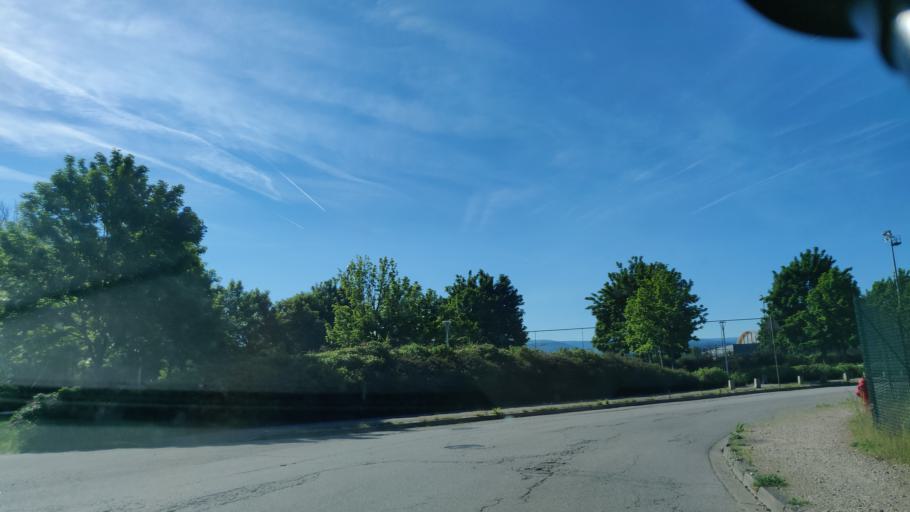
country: FR
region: Lorraine
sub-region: Departement des Vosges
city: Saint-Die-des-Vosges
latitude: 48.2853
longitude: 6.9680
